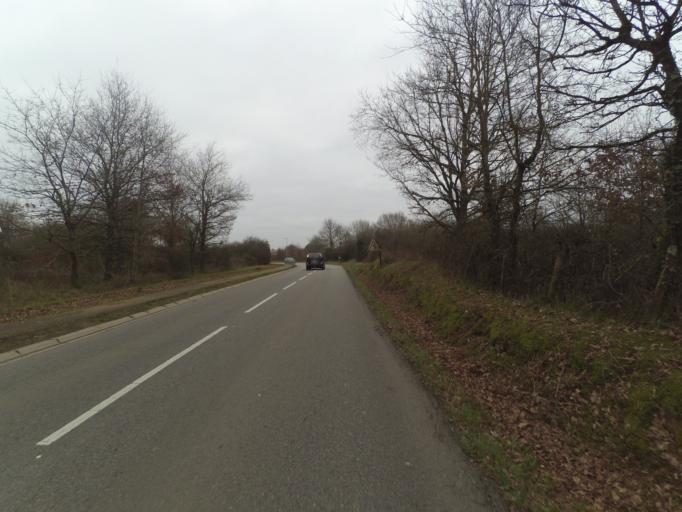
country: FR
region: Pays de la Loire
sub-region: Departement de la Loire-Atlantique
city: Saint-Herblain
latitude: 47.2201
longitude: -1.6580
